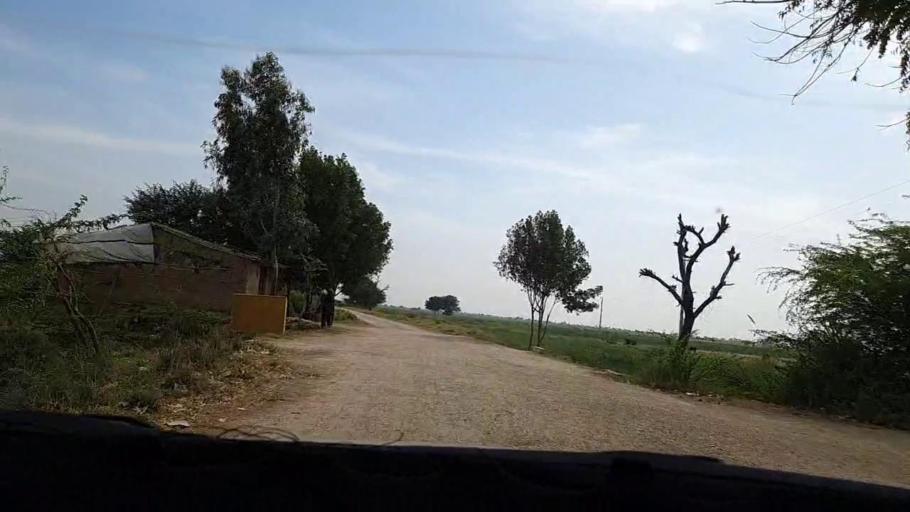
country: PK
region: Sindh
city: Pithoro
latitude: 25.5500
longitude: 69.3293
